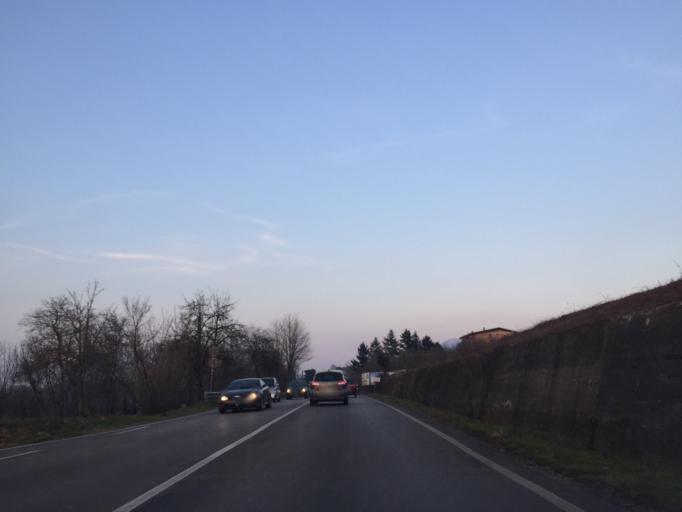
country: IT
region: Campania
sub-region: Provincia di Avellino
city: Avellino
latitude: 40.9006
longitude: 14.8004
